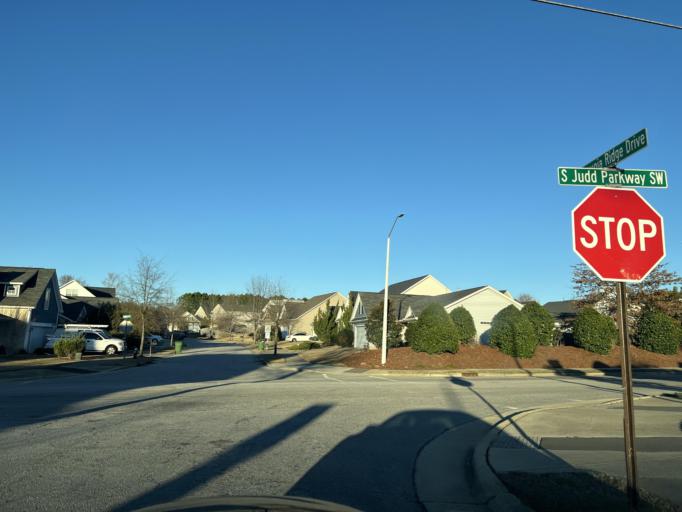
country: US
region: North Carolina
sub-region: Wake County
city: Fuquay-Varina
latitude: 35.5747
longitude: -78.8088
